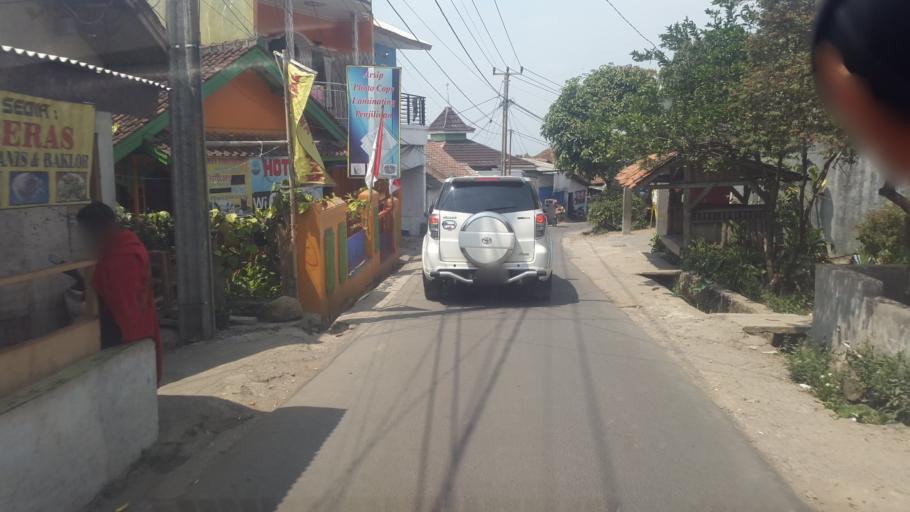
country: ID
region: West Java
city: Cicurug
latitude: -6.7755
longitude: 106.7393
